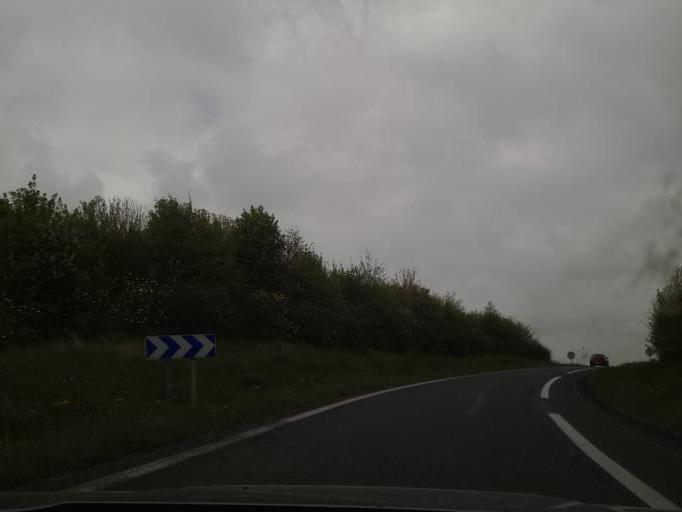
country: FR
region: Pays de la Loire
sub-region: Departement de la Vendee
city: Fontenay-le-Comte
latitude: 46.4333
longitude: -0.8173
